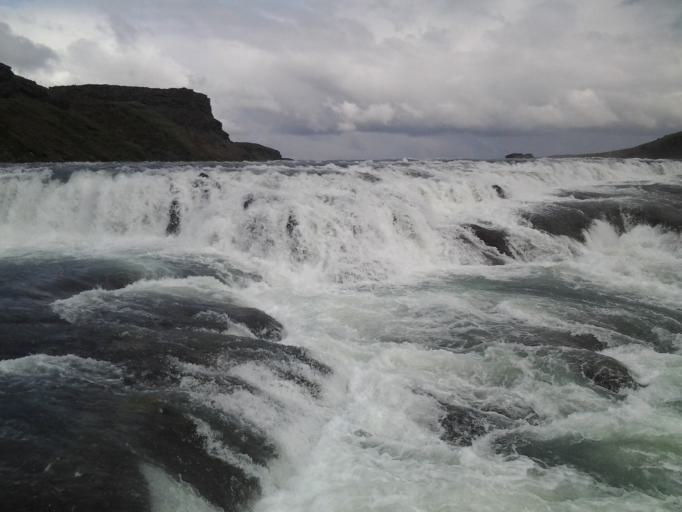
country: IS
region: South
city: Vestmannaeyjar
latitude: 64.3271
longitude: -20.1210
